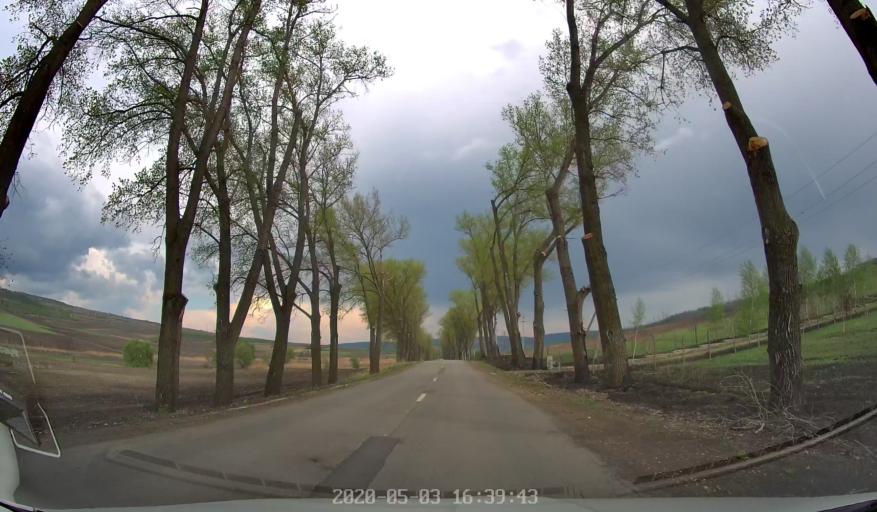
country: MD
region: Stinga Nistrului
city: Bucovat
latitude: 47.1807
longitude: 28.3796
